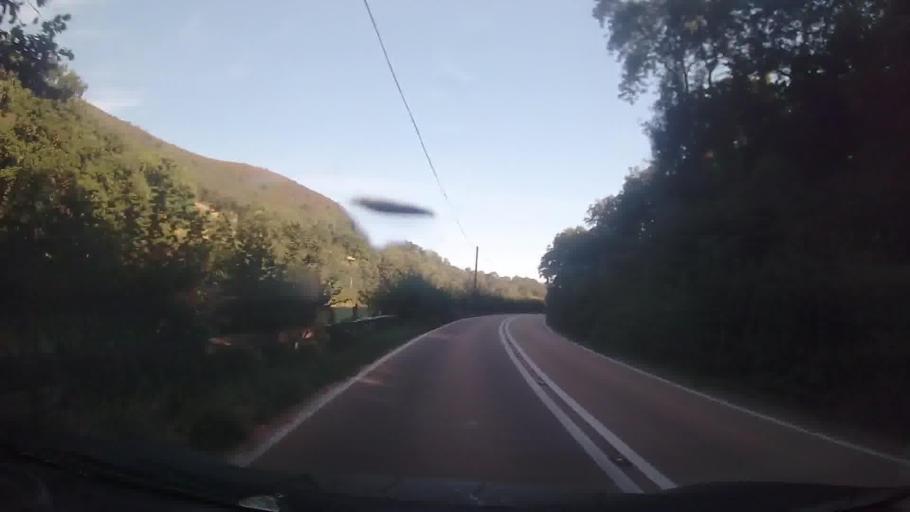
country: GB
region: Wales
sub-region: Blaenau Gwent
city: Brynmawr
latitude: 51.9113
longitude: -3.1922
